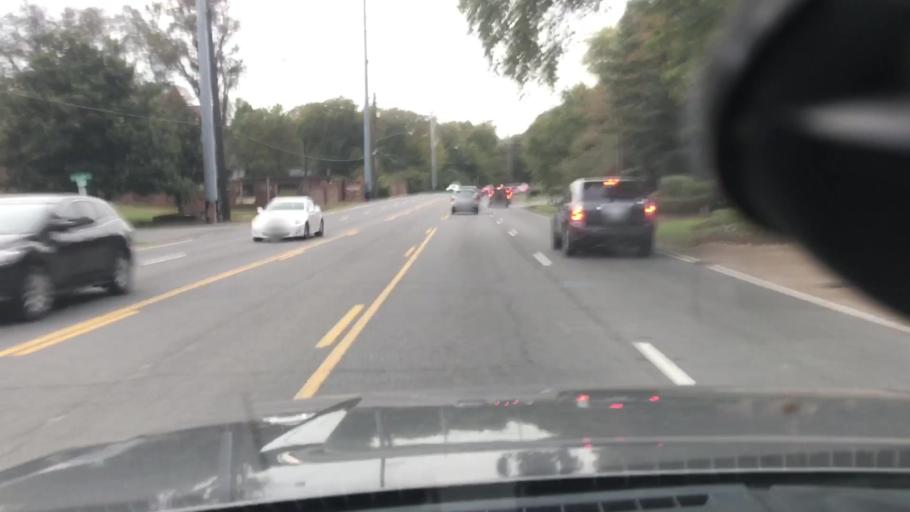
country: US
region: Tennessee
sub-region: Davidson County
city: Oak Hill
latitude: 36.1157
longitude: -86.8106
